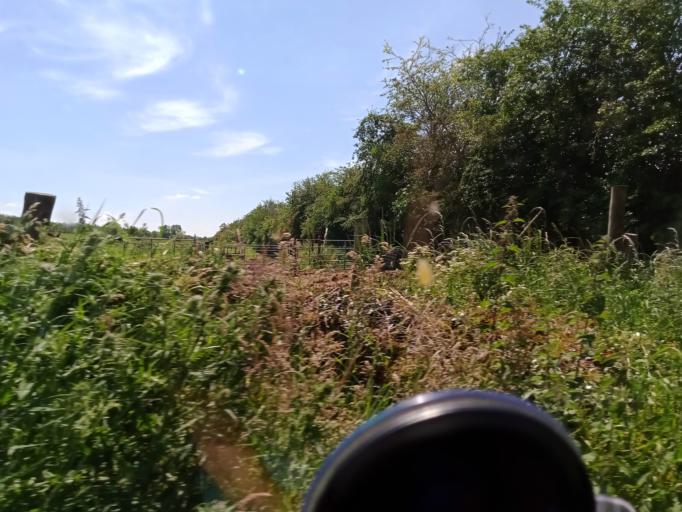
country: IE
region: Leinster
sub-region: Kilkenny
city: Thomastown
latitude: 52.5545
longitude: -7.0982
